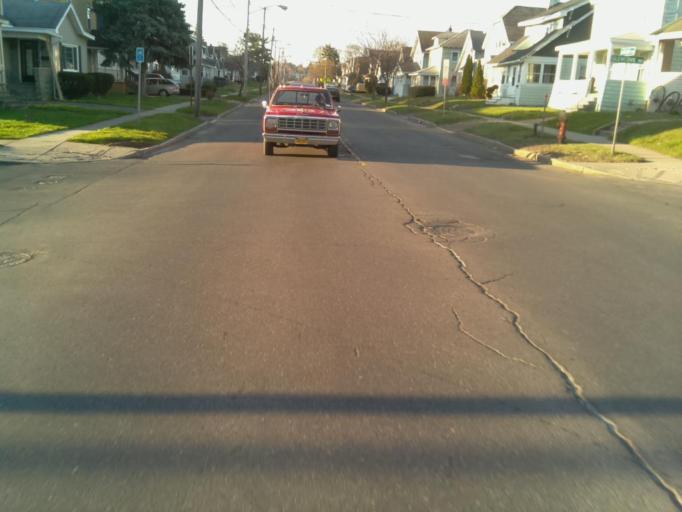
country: US
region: New York
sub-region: Onondaga County
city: East Syracuse
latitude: 43.0641
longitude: -76.1044
